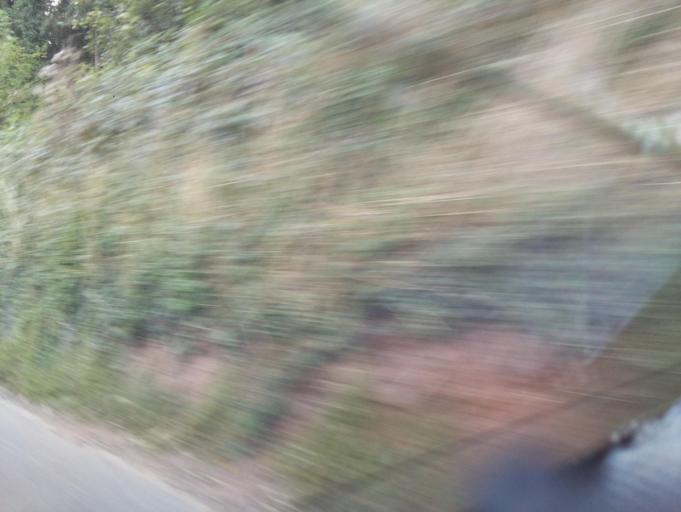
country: GB
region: England
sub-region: Devon
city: Tiverton
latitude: 50.8725
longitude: -3.4956
